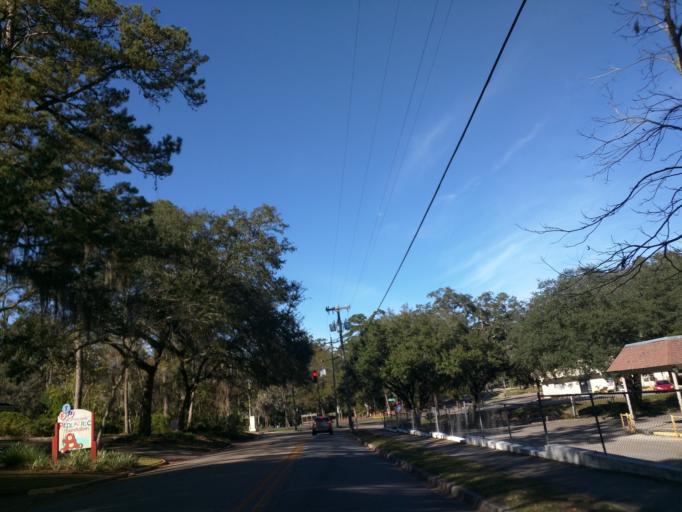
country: US
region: Florida
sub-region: Leon County
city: Tallahassee
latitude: 30.4557
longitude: -84.2640
